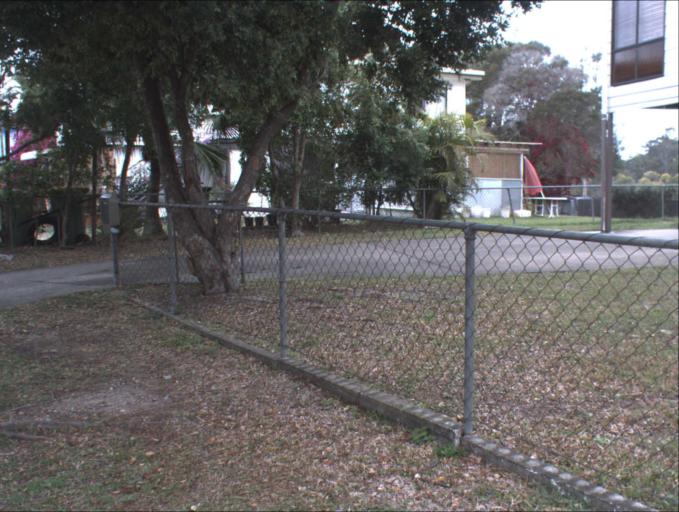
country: AU
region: Queensland
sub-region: Logan
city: Waterford West
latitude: -27.6877
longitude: 153.1152
